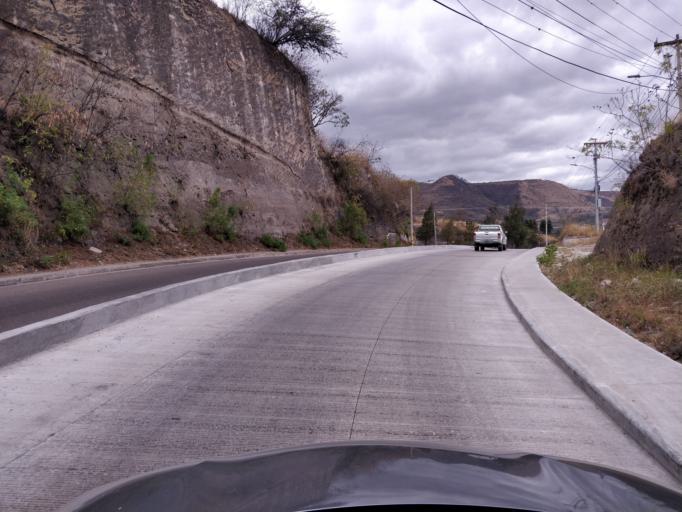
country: HN
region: Francisco Morazan
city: Tegucigalpa
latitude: 14.0502
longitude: -87.2132
